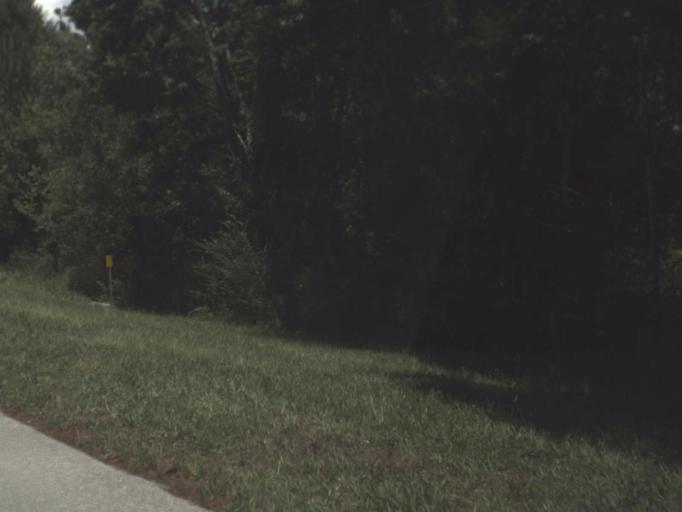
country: US
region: Florida
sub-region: Baker County
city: Macclenny
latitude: 30.1537
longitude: -82.1852
